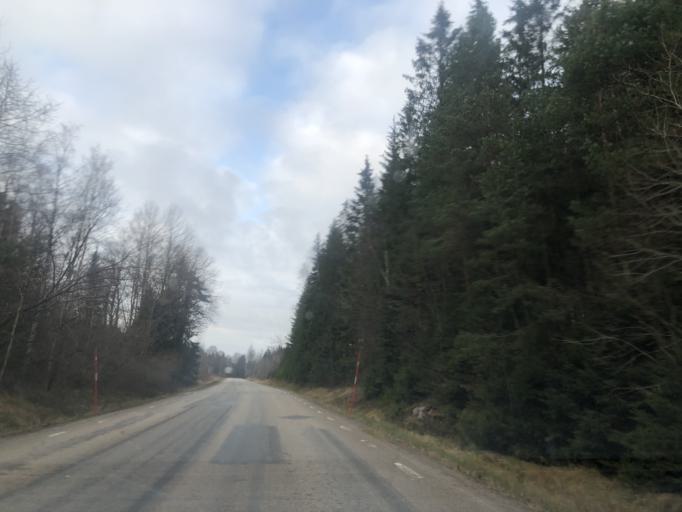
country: SE
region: Vaestra Goetaland
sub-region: Tranemo Kommun
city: Langhem
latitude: 57.7074
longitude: 13.2982
